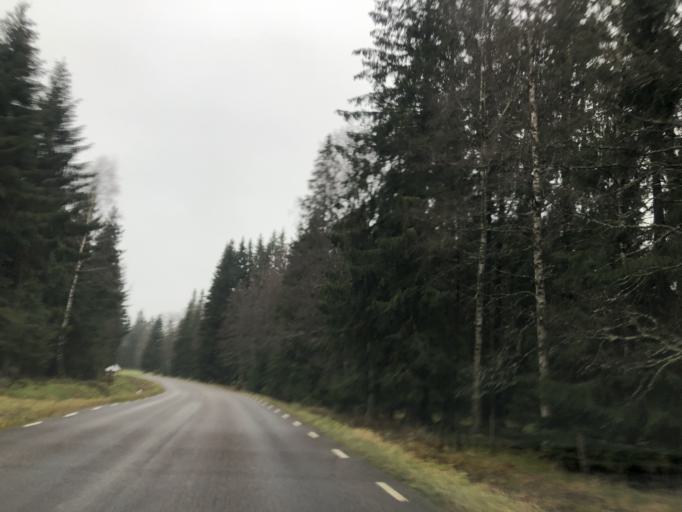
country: SE
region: Vaestra Goetaland
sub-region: Ulricehamns Kommun
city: Ulricehamn
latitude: 57.7618
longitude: 13.4811
